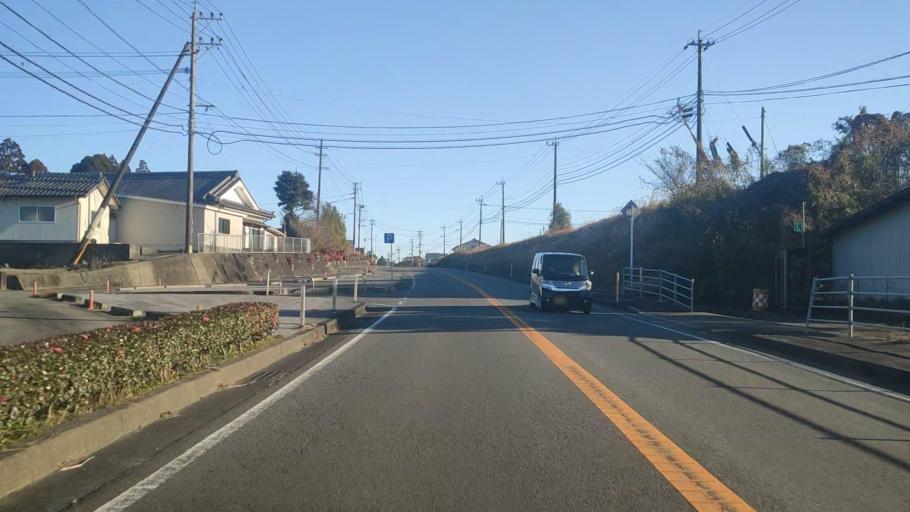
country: JP
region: Miyazaki
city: Takanabe
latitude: 32.3126
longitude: 131.5874
